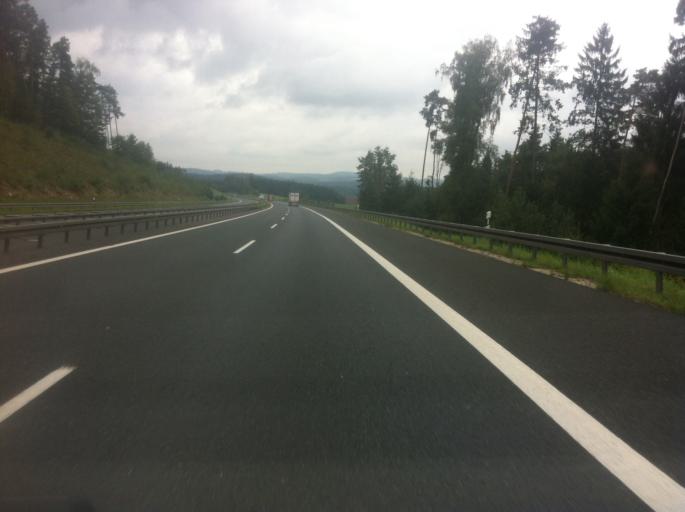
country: DE
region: Bavaria
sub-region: Upper Palatinate
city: Wernberg-Koblitz
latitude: 49.5587
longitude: 12.2005
